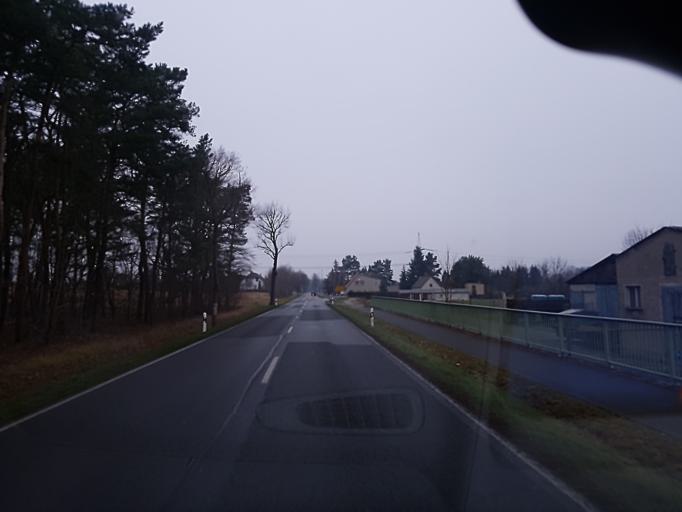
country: DE
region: Brandenburg
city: Lubbenau
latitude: 51.8804
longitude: 13.9072
